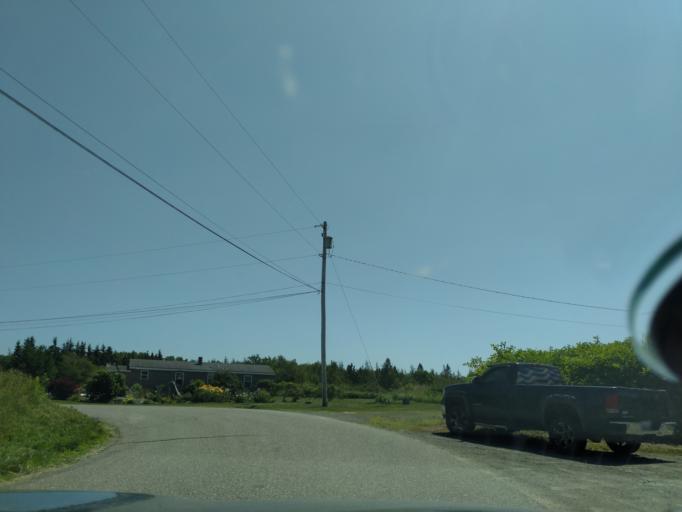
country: US
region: Maine
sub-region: Washington County
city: Eastport
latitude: 44.8294
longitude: -67.0046
